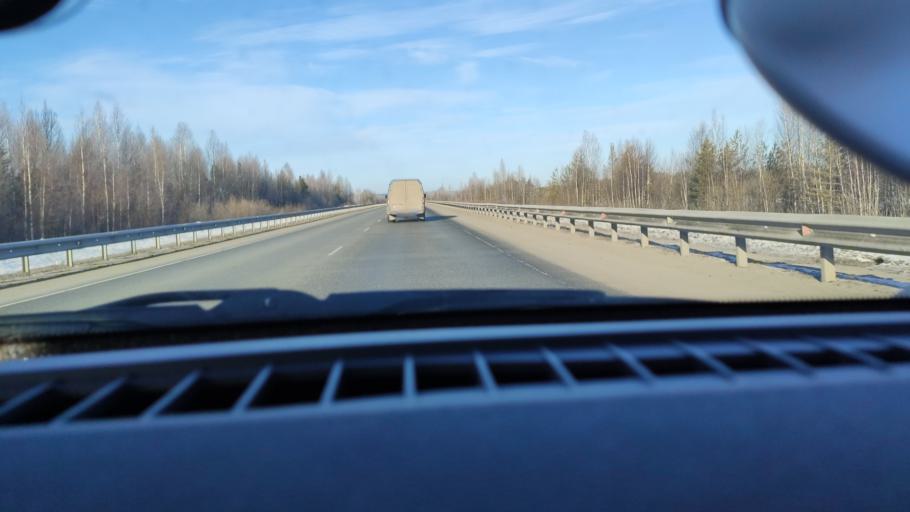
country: RU
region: Perm
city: Krasnokamsk
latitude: 58.0889
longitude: 55.6878
